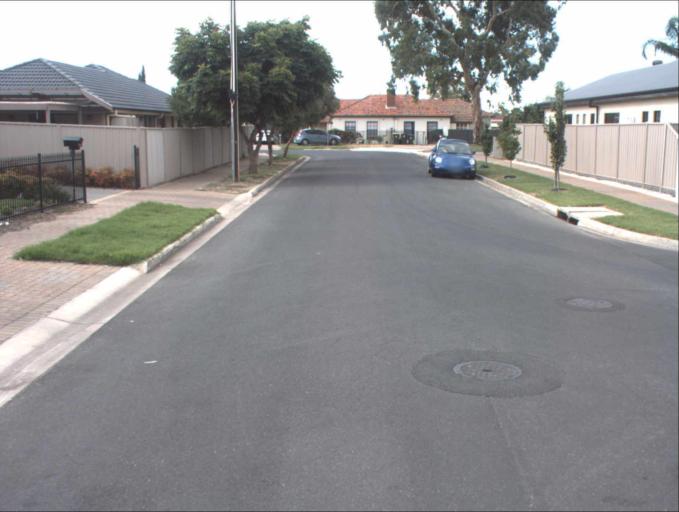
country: AU
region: South Australia
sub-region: Prospect
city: Prospect
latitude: -34.8698
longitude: 138.5877
